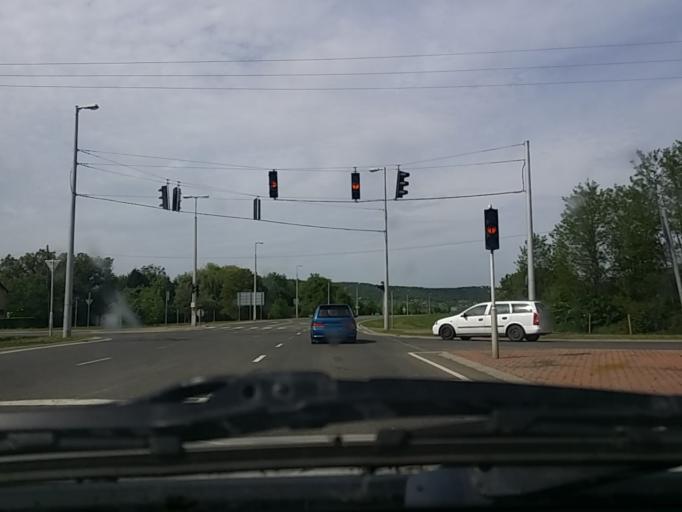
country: HU
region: Baranya
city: Harkany
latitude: 45.8564
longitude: 18.2233
